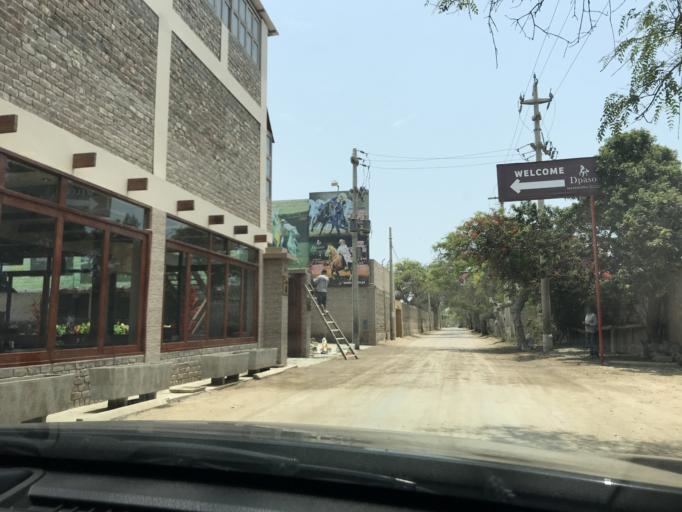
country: PE
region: Lima
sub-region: Lima
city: Punta Hermosa
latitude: -12.2556
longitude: -76.9133
